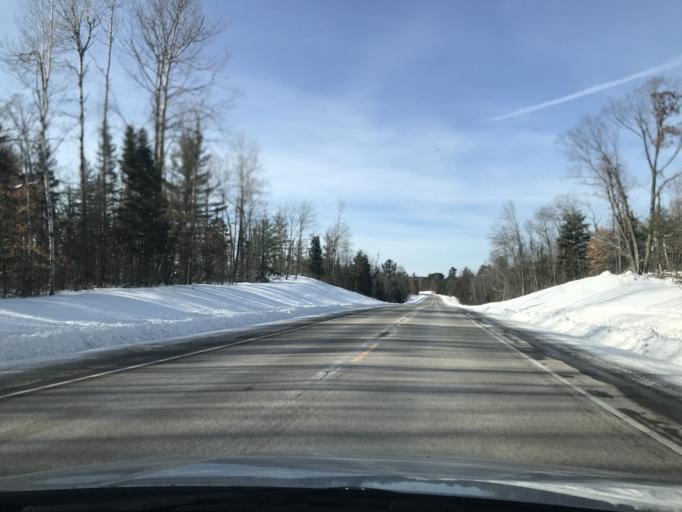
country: US
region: Wisconsin
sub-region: Oconto County
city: Gillett
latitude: 45.1245
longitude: -88.3981
